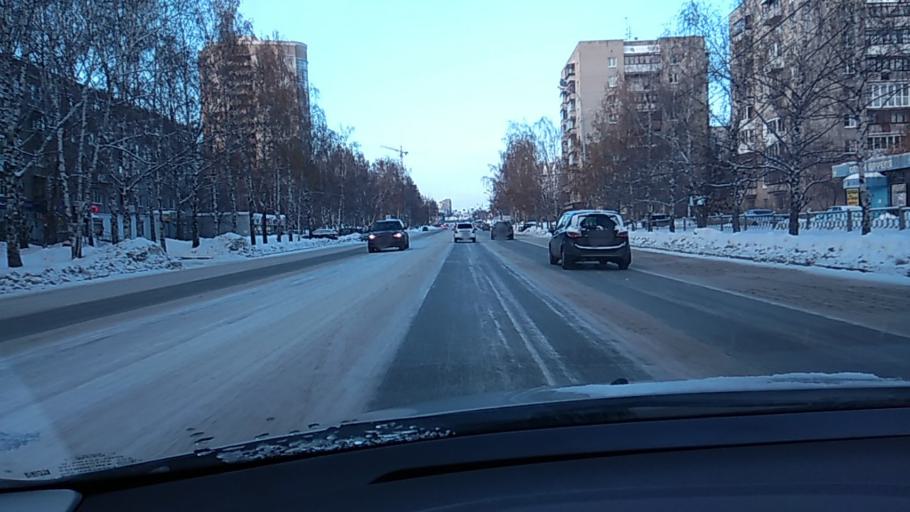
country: RU
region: Sverdlovsk
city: Sovkhoznyy
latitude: 56.8177
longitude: 60.5616
